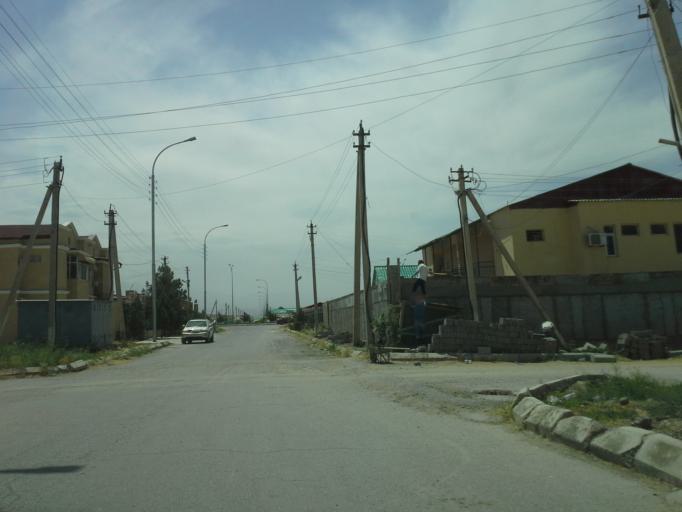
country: TM
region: Ahal
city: Ashgabat
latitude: 37.9961
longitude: 58.4104
